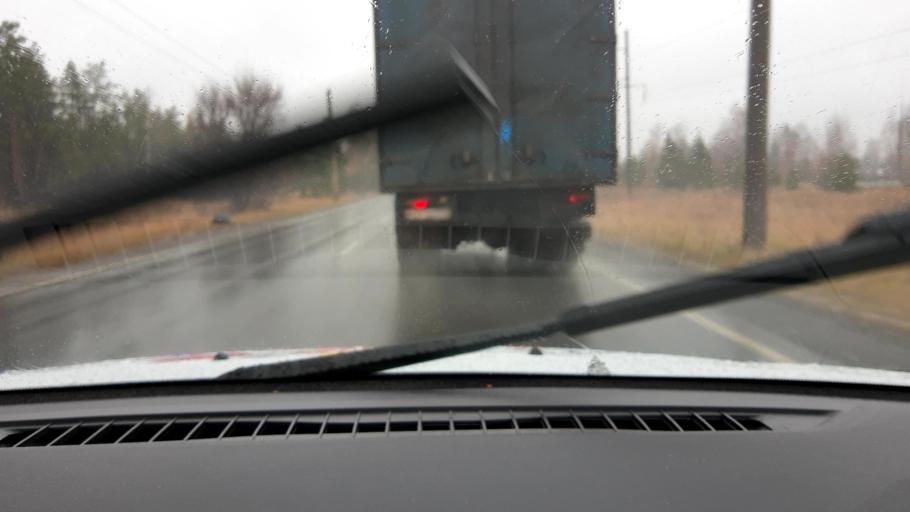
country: RU
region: Nizjnij Novgorod
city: Babino
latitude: 56.2860
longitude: 43.5843
